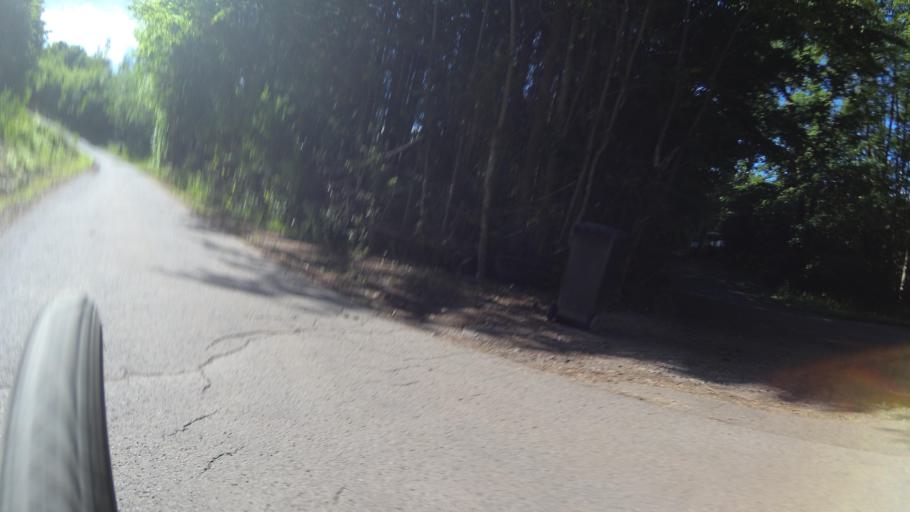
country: DE
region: Saarland
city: Eppelborn
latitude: 49.3535
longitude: 6.9838
